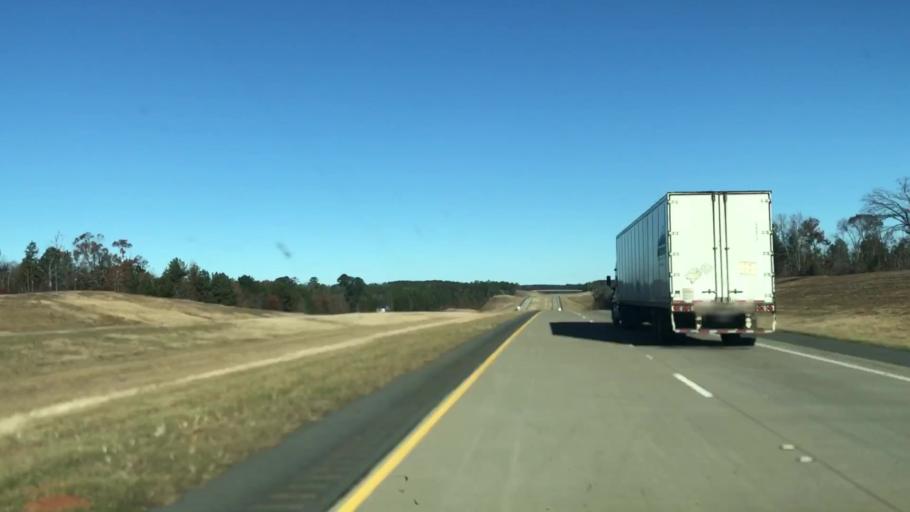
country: US
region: Louisiana
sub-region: Caddo Parish
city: Vivian
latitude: 32.9593
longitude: -93.9024
